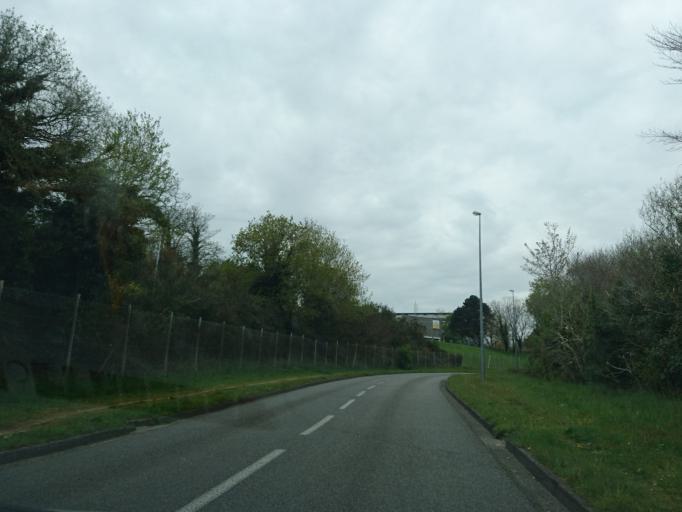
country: FR
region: Brittany
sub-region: Departement du Finistere
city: Roscanvel
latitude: 48.3620
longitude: -4.5611
